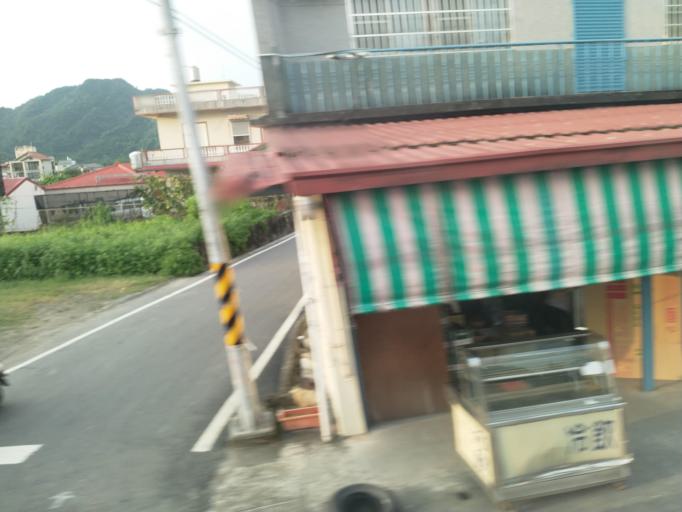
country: TW
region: Taiwan
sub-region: Pingtung
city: Pingtung
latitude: 22.8855
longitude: 120.5089
